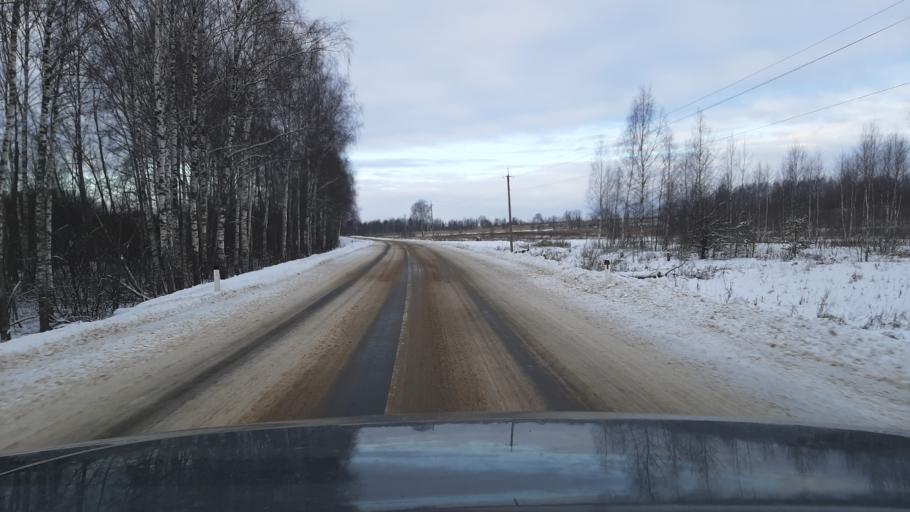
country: RU
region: Kostroma
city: Nerekhta
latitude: 57.4725
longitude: 40.6552
